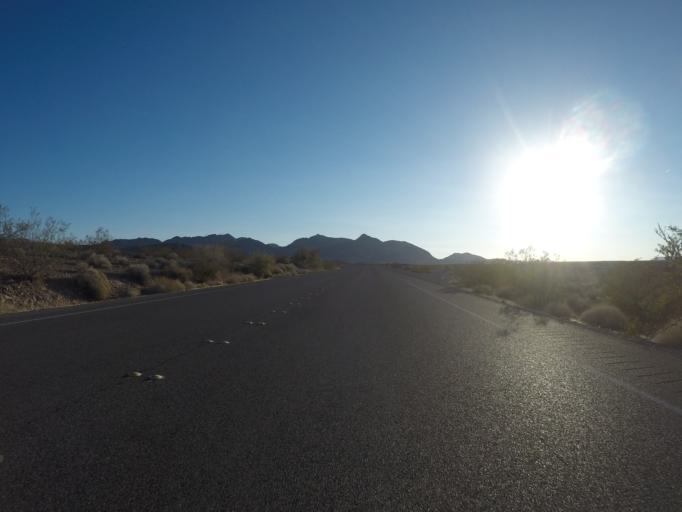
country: US
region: Nevada
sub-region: Clark County
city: Moapa Valley
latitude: 36.2868
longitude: -114.4890
